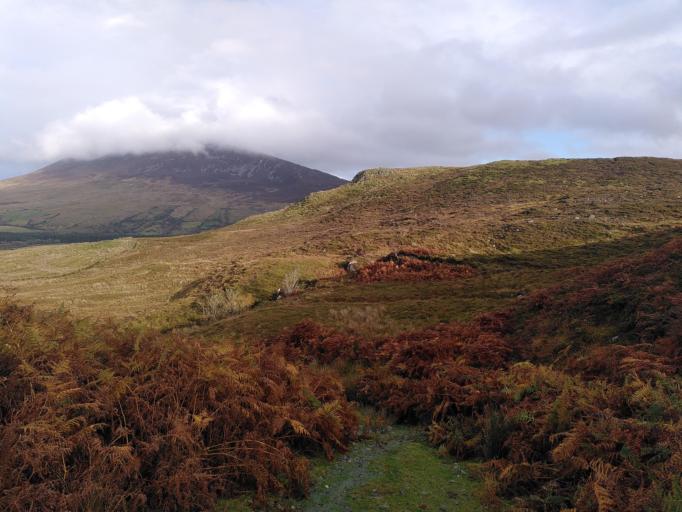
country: IE
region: Connaught
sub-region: Maigh Eo
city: Crossmolina
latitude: 53.9877
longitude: -9.4277
